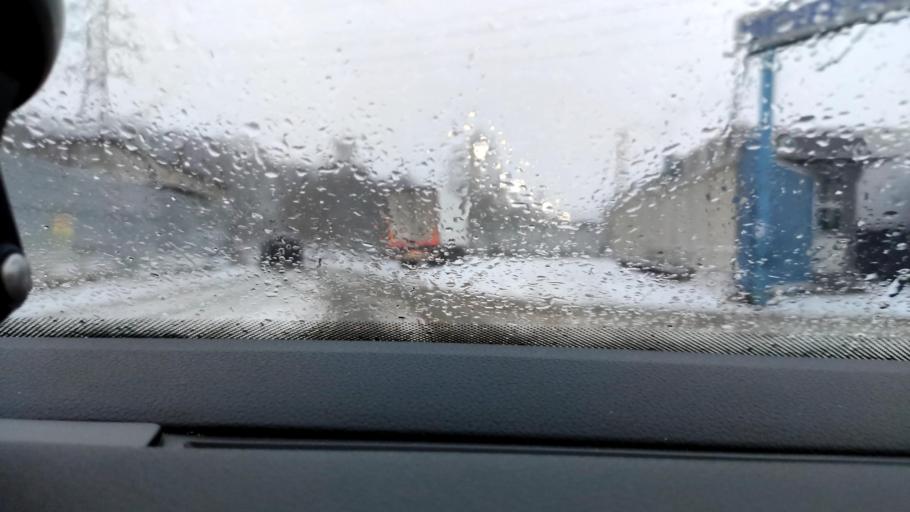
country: RU
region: Moskovskaya
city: Razvilka
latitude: 55.5911
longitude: 37.7477
